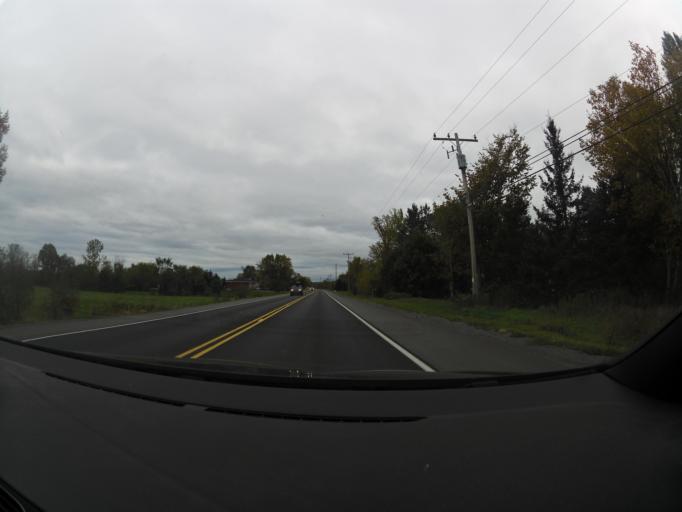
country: CA
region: Ontario
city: Bells Corners
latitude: 45.3970
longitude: -75.9896
